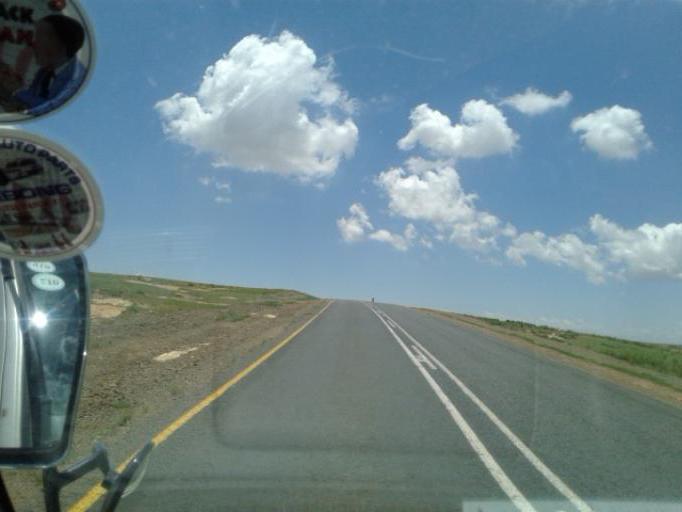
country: LS
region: Maseru
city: Maseru
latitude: -29.3019
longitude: 27.6111
